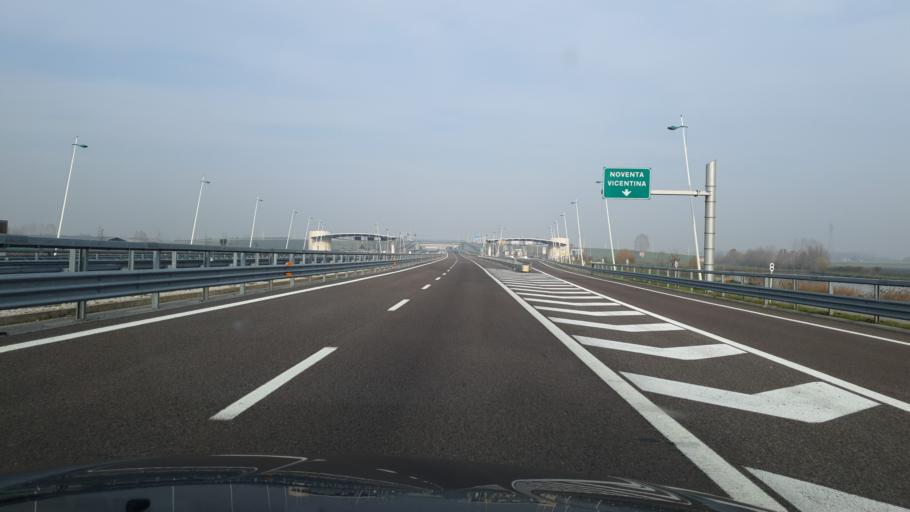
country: IT
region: Veneto
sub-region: Provincia di Vicenza
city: Noventa Vicentina
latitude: 45.2675
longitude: 11.5718
